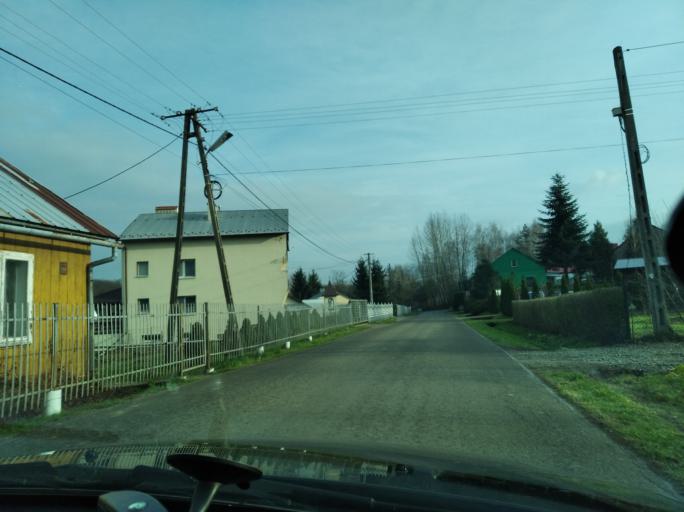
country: PL
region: Subcarpathian Voivodeship
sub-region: Powiat przeworski
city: Siedleczka
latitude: 49.9654
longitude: 22.3710
